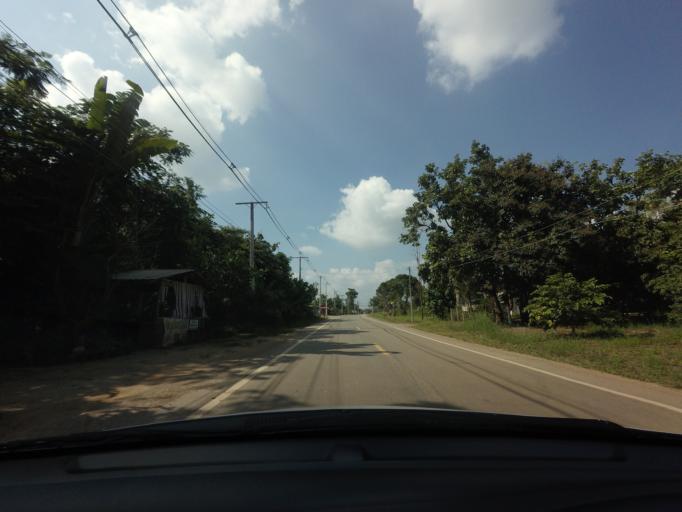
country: TH
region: Nakhon Ratchasima
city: Wang Nam Khiao
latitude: 14.4410
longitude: 101.6750
